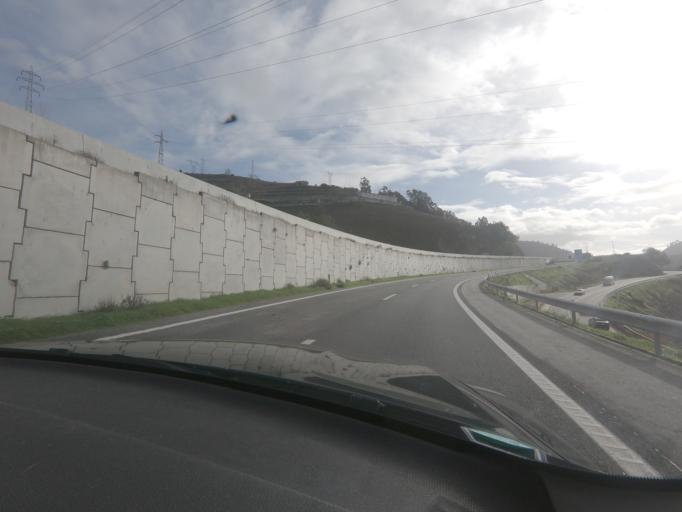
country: PT
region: Vila Real
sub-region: Peso da Regua
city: Peso da Regua
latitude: 41.1406
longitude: -7.7725
